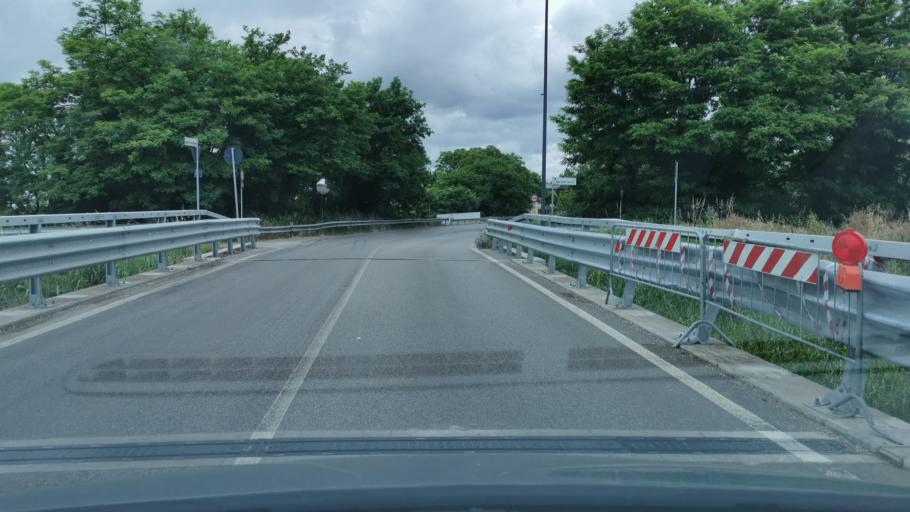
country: IT
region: Emilia-Romagna
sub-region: Provincia di Ravenna
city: Madonna Dell'Albero
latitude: 44.3963
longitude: 12.1970
